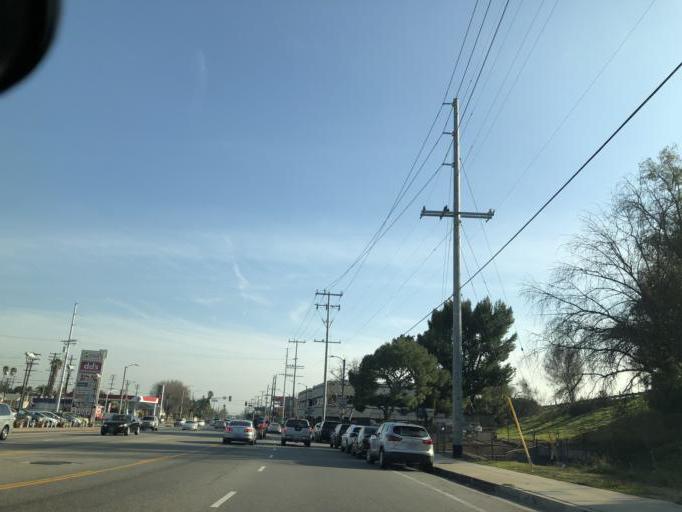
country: US
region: California
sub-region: Los Angeles County
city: San Fernando
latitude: 34.2810
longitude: -118.4558
